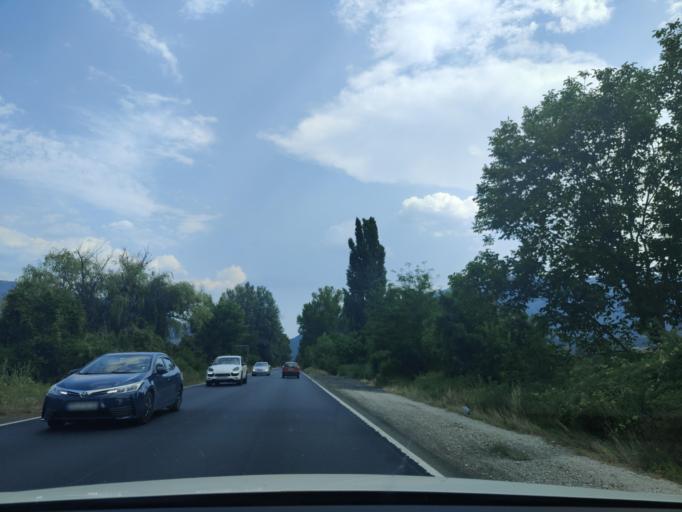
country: BG
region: Blagoevgrad
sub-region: Obshtina Simitli
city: Simitli
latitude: 41.8669
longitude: 23.1272
